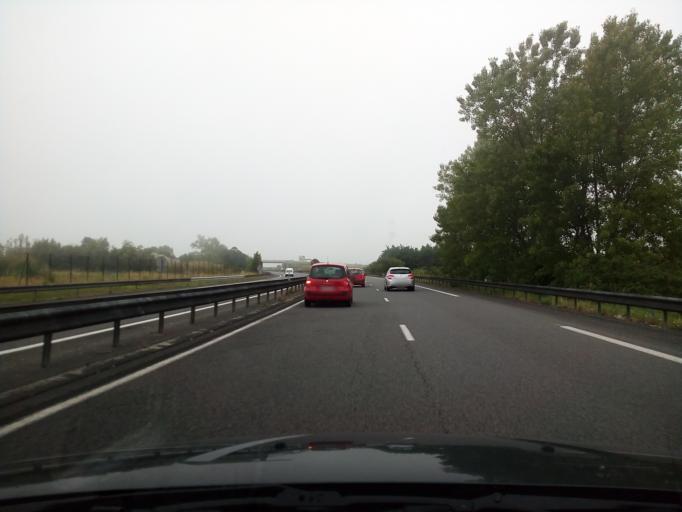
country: FR
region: Poitou-Charentes
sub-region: Departement de la Charente
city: Jarnac
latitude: 45.6956
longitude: -0.1335
